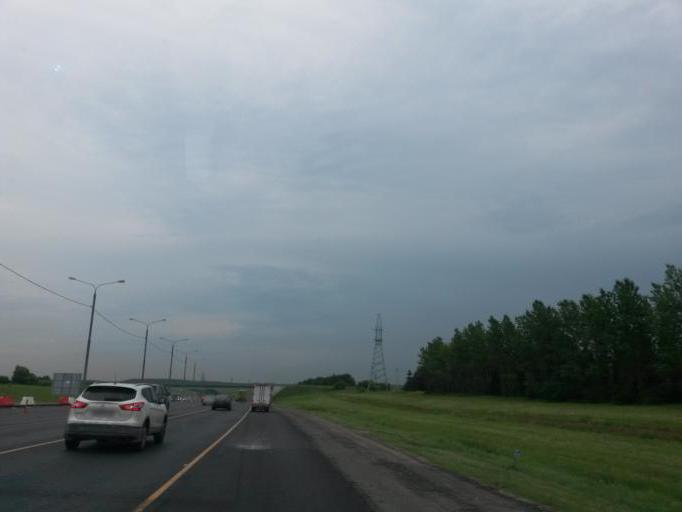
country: RU
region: Moskovskaya
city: Klimovsk
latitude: 55.3418
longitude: 37.5839
